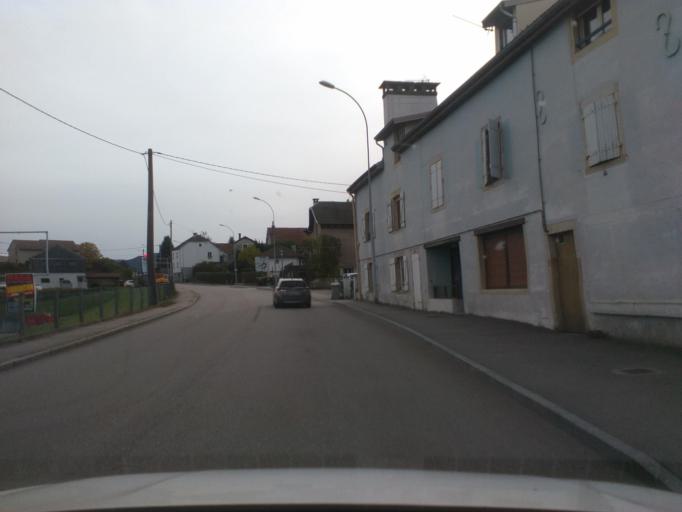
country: FR
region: Lorraine
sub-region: Departement des Vosges
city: Saint-Etienne-les-Remiremont
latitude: 48.0103
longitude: 6.6028
